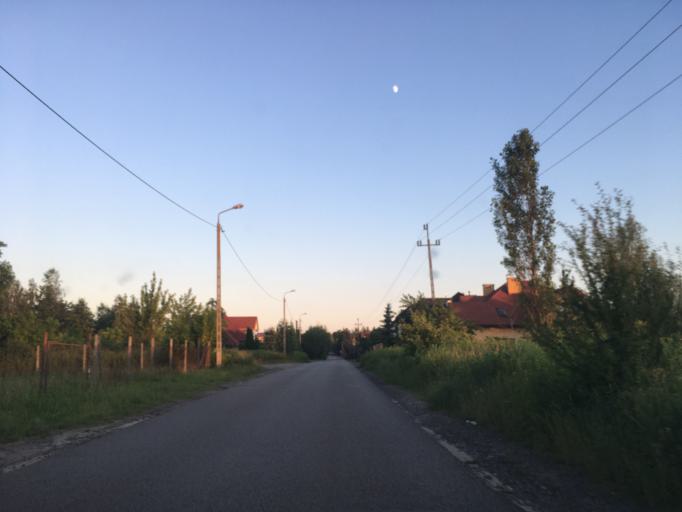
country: PL
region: Masovian Voivodeship
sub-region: Powiat piaseczynski
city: Piaseczno
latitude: 52.0698
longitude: 21.0106
